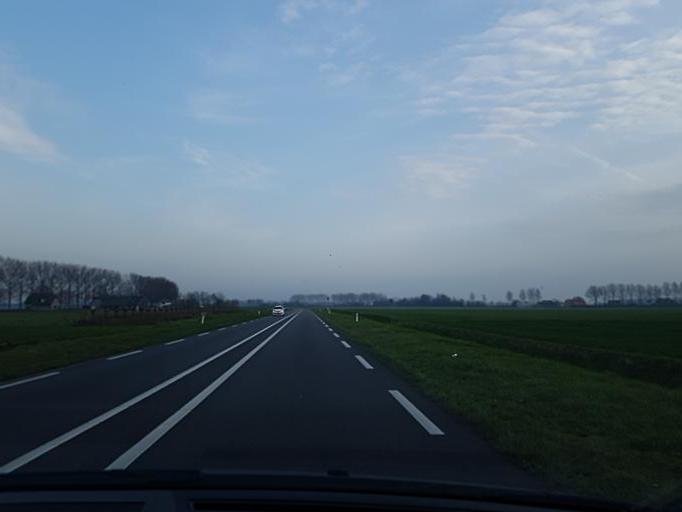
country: NL
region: Zeeland
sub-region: Gemeente Hulst
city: Hulst
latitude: 51.3128
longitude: 4.0358
